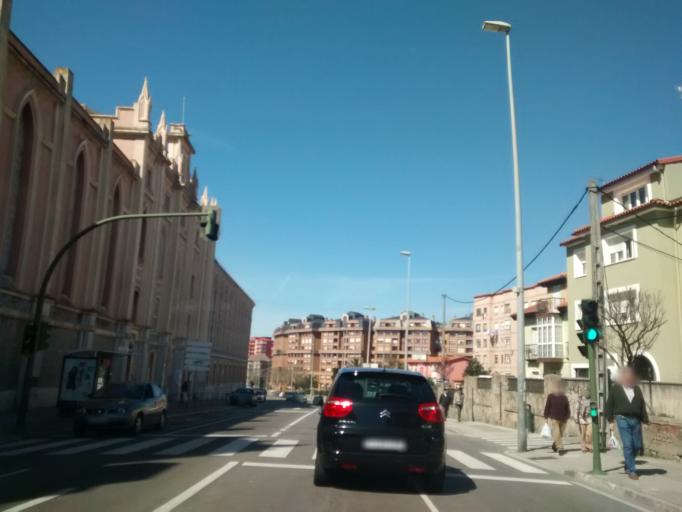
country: ES
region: Cantabria
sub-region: Provincia de Cantabria
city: Santander
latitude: 43.4674
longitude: -3.8083
